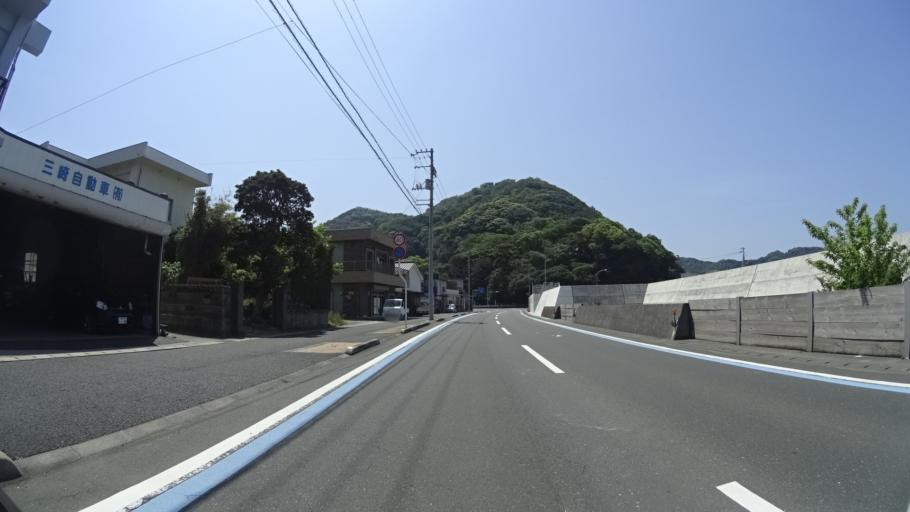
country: JP
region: Ehime
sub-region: Nishiuwa-gun
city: Ikata-cho
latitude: 33.3891
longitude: 132.1207
